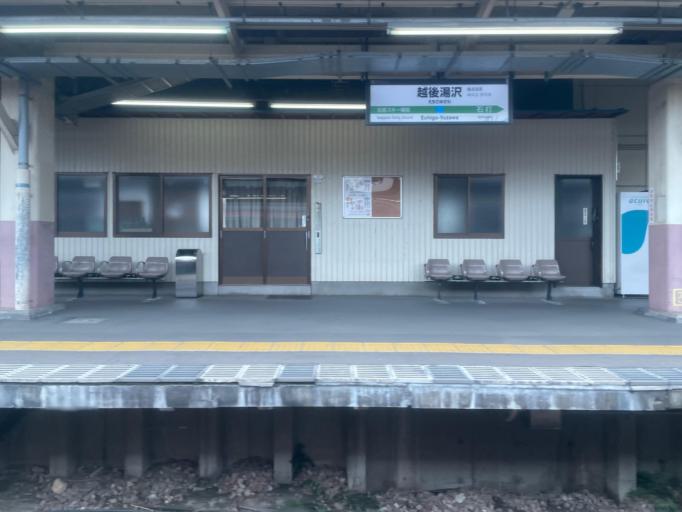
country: JP
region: Niigata
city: Shiozawa
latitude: 36.9358
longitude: 138.8101
